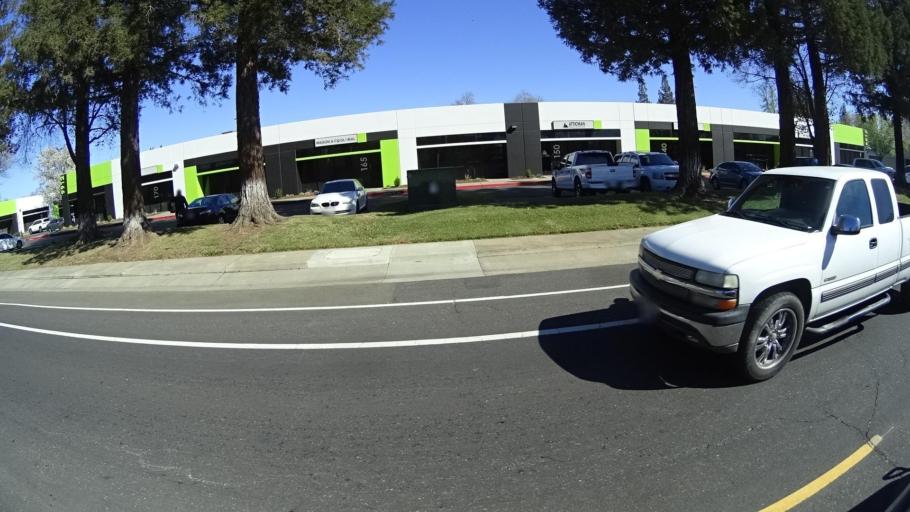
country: US
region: California
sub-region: Sacramento County
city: La Riviera
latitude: 38.5731
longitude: -121.3284
